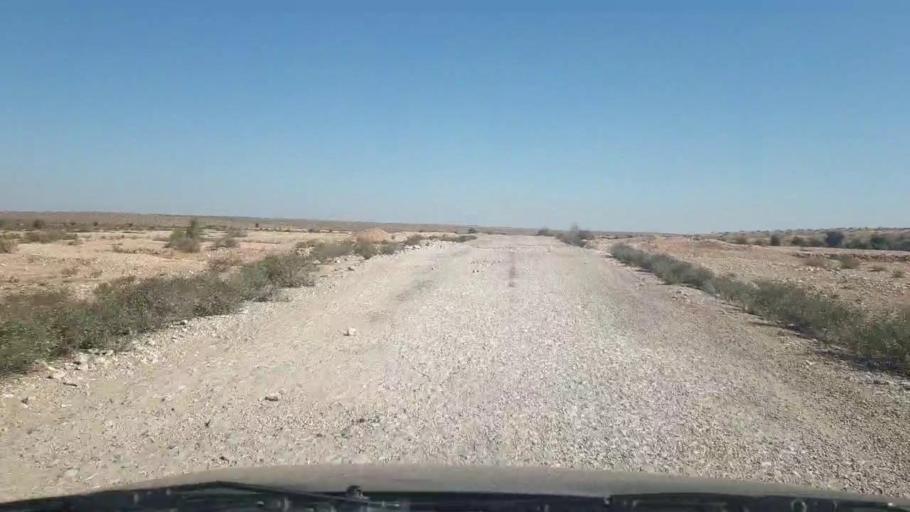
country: PK
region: Sindh
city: Bozdar
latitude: 27.0171
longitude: 68.7583
